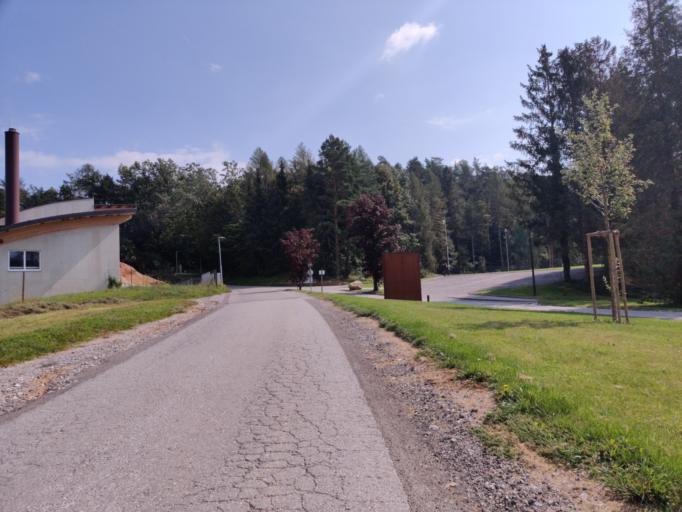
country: AT
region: Styria
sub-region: Graz Stadt
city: Mariatrost
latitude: 47.1277
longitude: 15.5017
